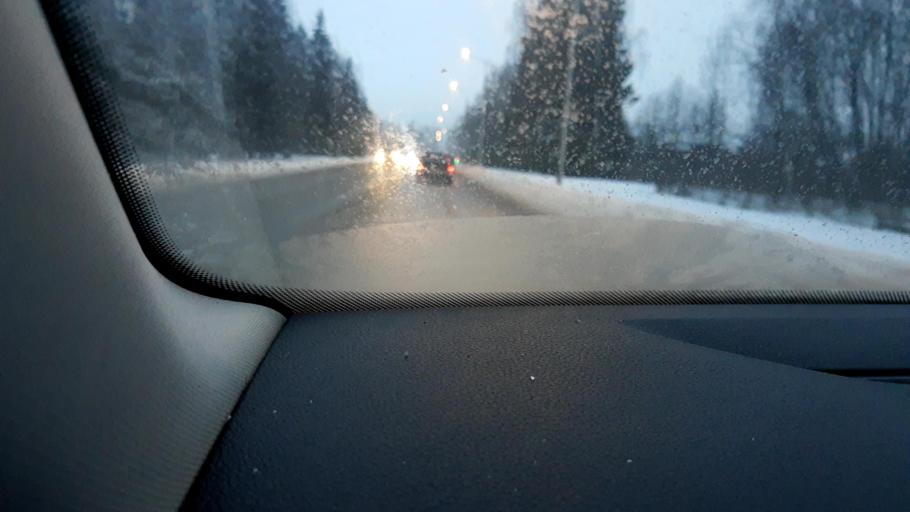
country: RU
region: Moskovskaya
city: Troitsk
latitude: 55.3023
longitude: 37.1996
